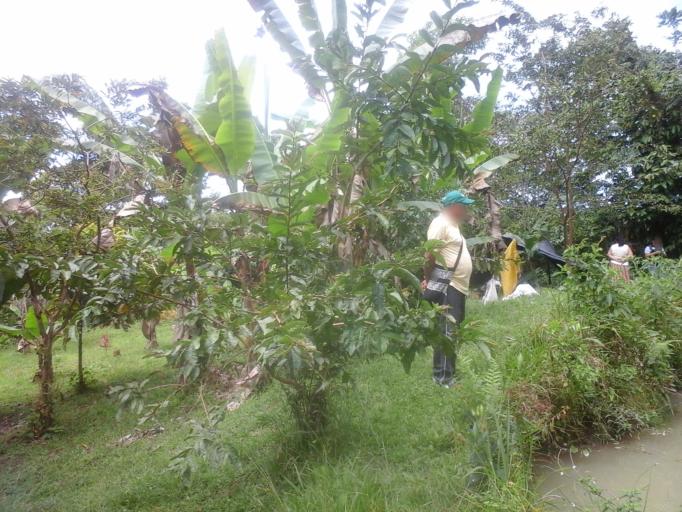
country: CO
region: Putumayo
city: Mocoa
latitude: 1.1836
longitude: -76.6773
